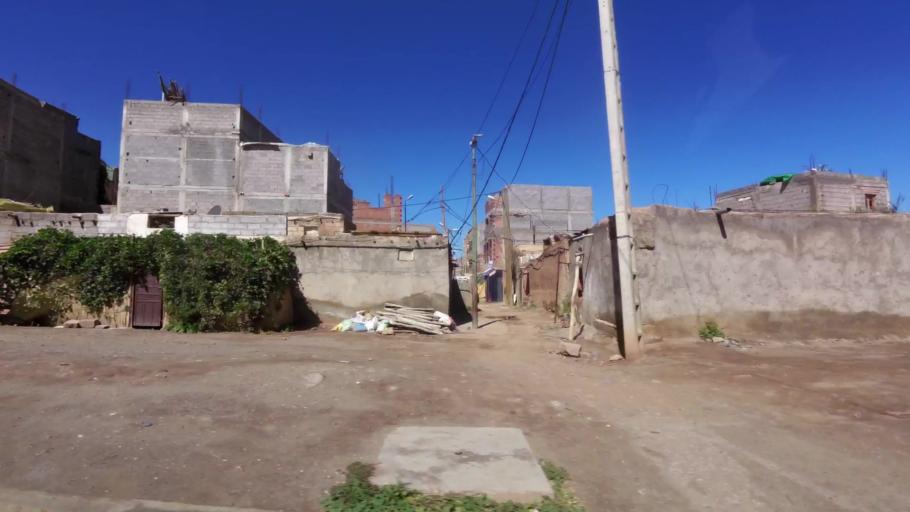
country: MA
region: Marrakech-Tensift-Al Haouz
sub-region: Marrakech
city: Marrakesh
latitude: 31.5905
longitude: -8.0561
